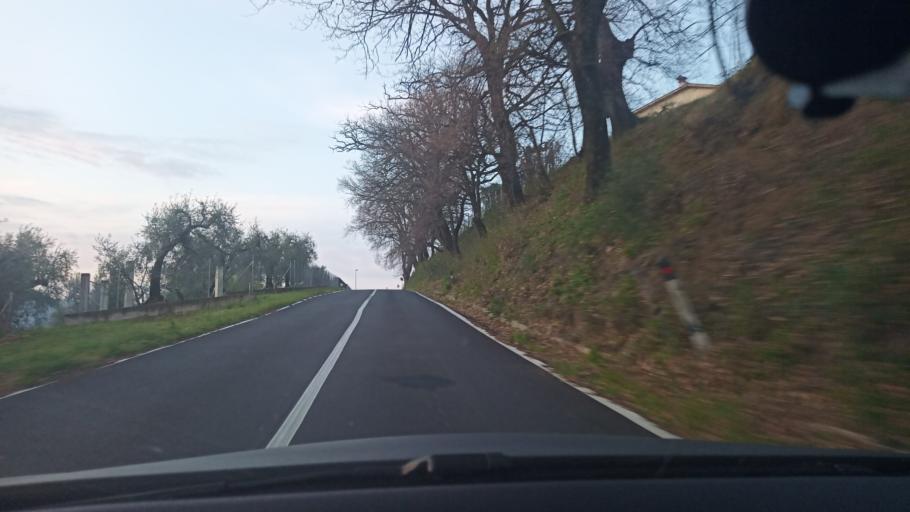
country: IT
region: Latium
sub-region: Provincia di Rieti
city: Torri in Sabina
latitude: 42.3450
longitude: 12.6509
